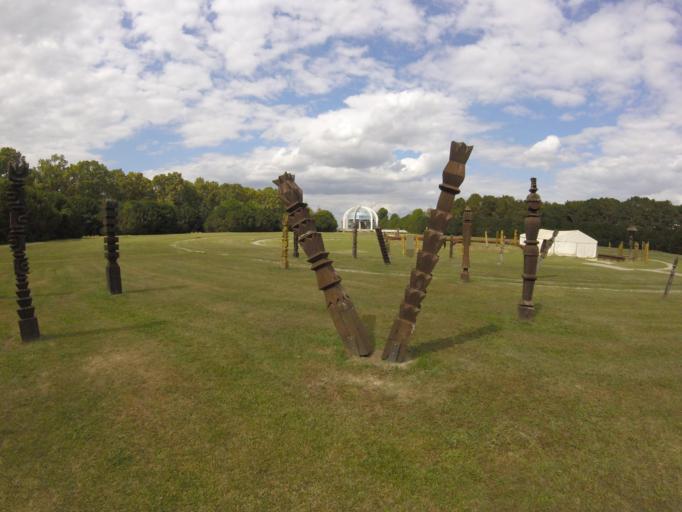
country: HU
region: Baranya
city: Mohacs
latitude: 45.9412
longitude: 18.6469
